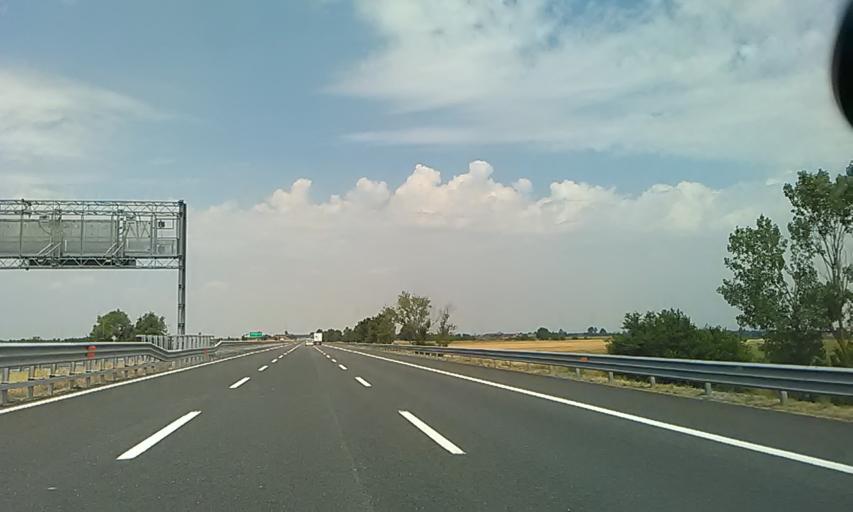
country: IT
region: Piedmont
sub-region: Provincia di Alessandria
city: Predosa
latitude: 44.7714
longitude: 8.6299
